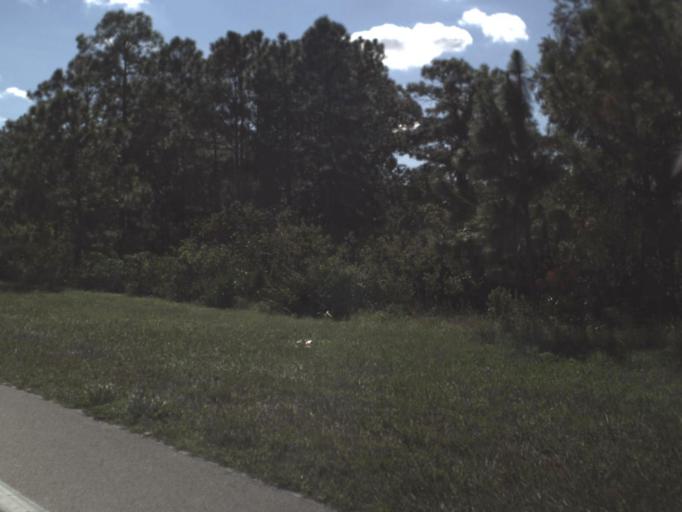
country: US
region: Florida
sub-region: Lee County
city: Lehigh Acres
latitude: 26.5151
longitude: -81.5508
